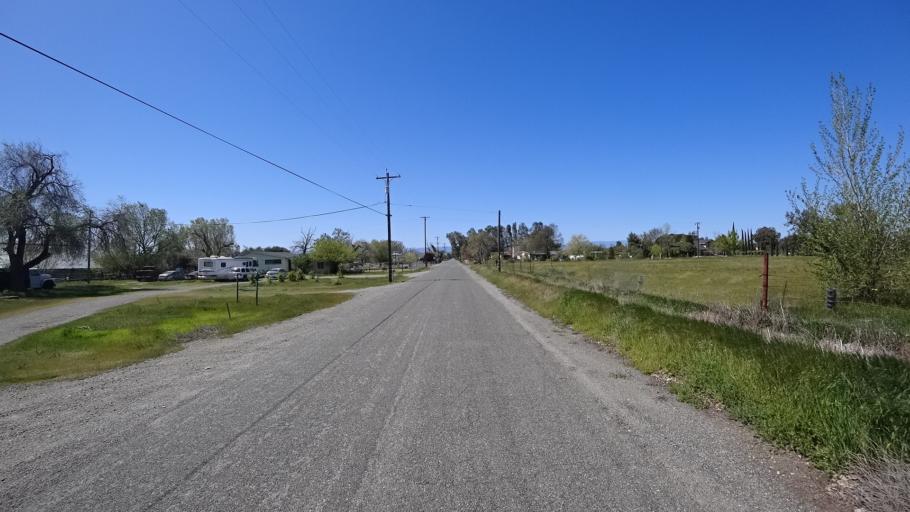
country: US
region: California
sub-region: Glenn County
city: Orland
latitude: 39.7768
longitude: -122.2374
